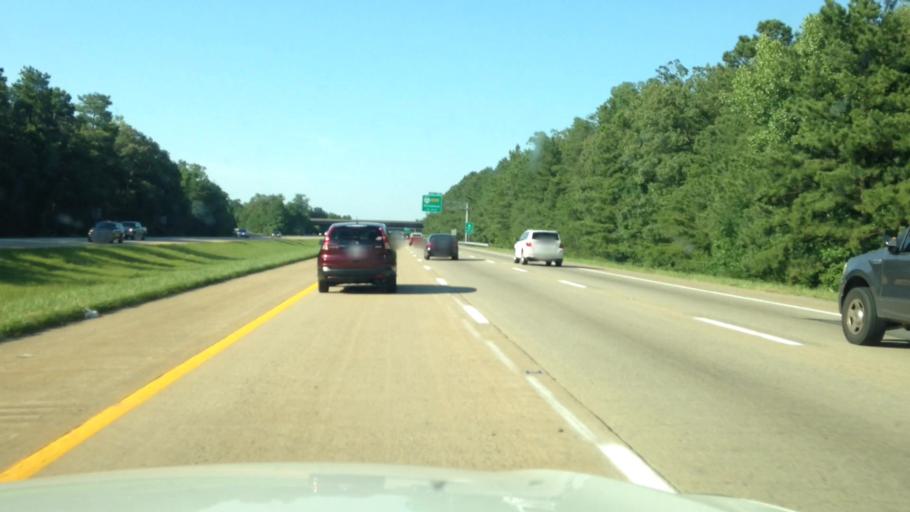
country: US
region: Virginia
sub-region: Henrico County
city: Fort Lee
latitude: 37.4662
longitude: -77.3104
